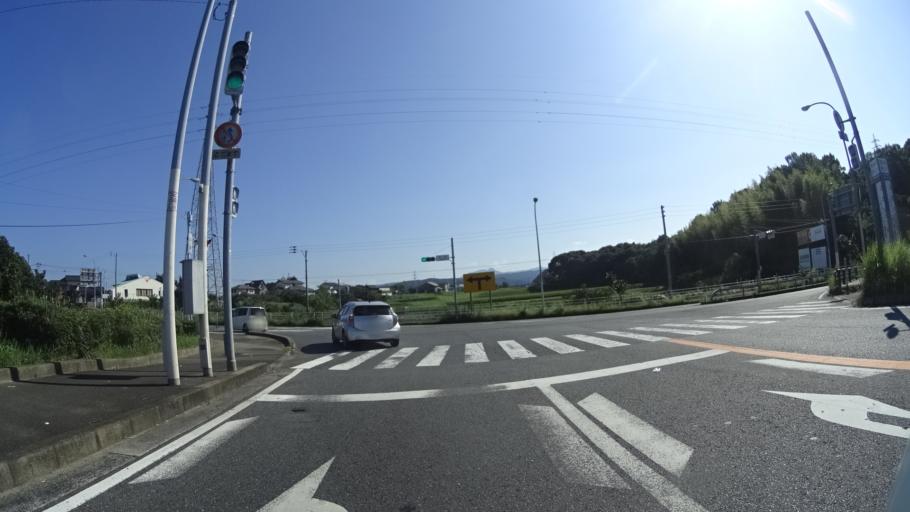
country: JP
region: Fukuoka
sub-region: Buzen-shi
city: Buzen
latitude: 33.6134
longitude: 131.1022
